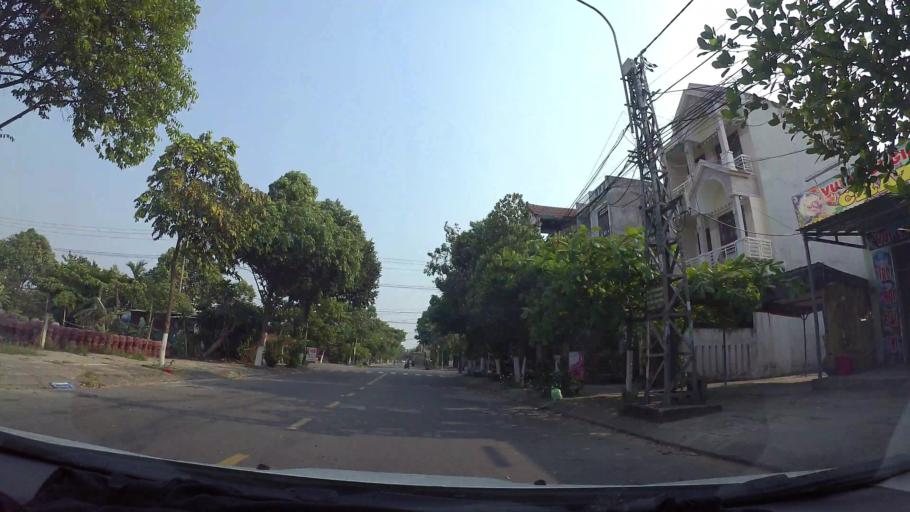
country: VN
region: Da Nang
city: Cam Le
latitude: 16.0219
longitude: 108.2064
